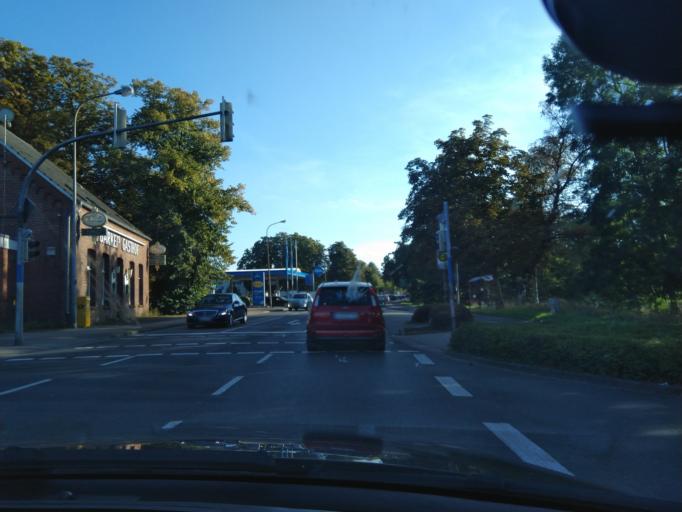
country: DE
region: Lower Saxony
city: Leer
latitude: 53.2483
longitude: 7.4581
